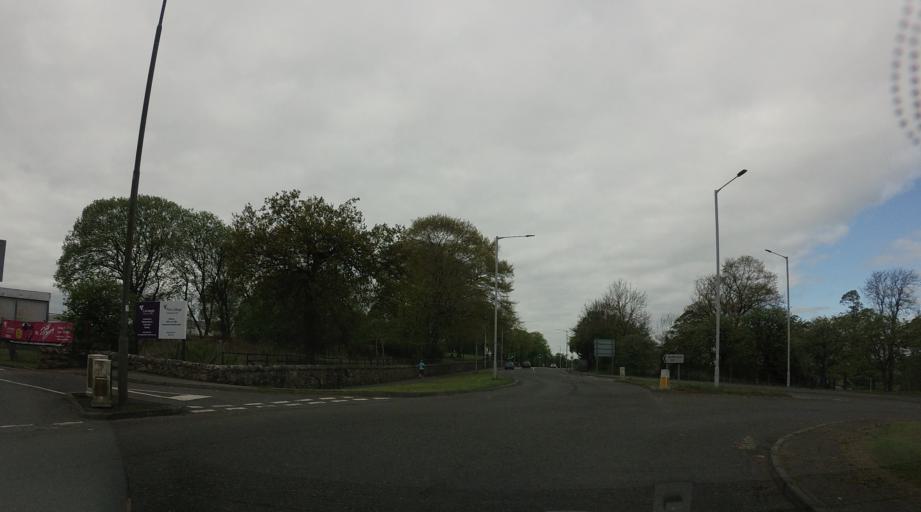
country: GB
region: Scotland
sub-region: Fife
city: Townhill
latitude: 56.0797
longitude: -3.4120
